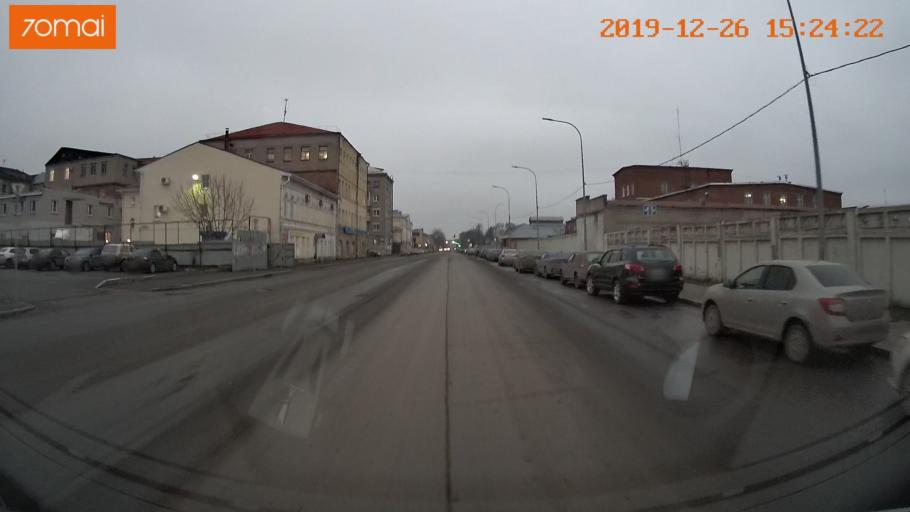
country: RU
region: Jaroslavl
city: Rybinsk
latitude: 58.0505
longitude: 38.8501
